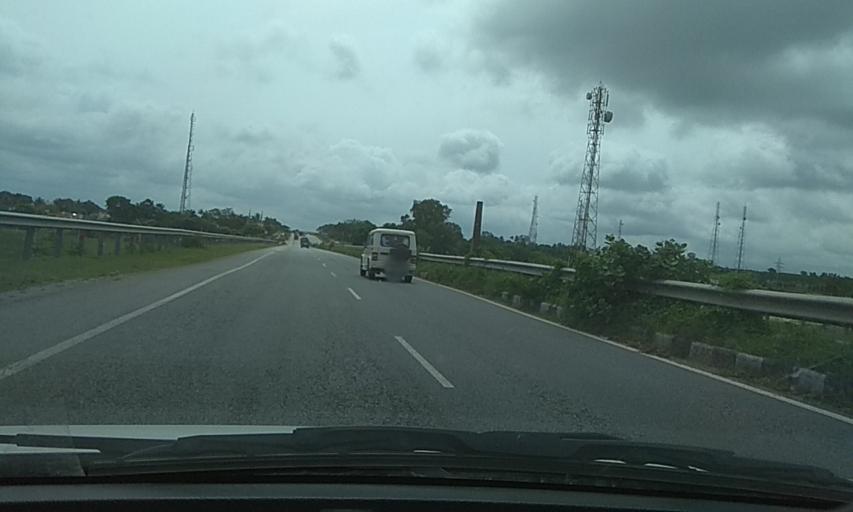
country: IN
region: Karnataka
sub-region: Davanagere
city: Mayakonda
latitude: 14.3948
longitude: 76.0387
